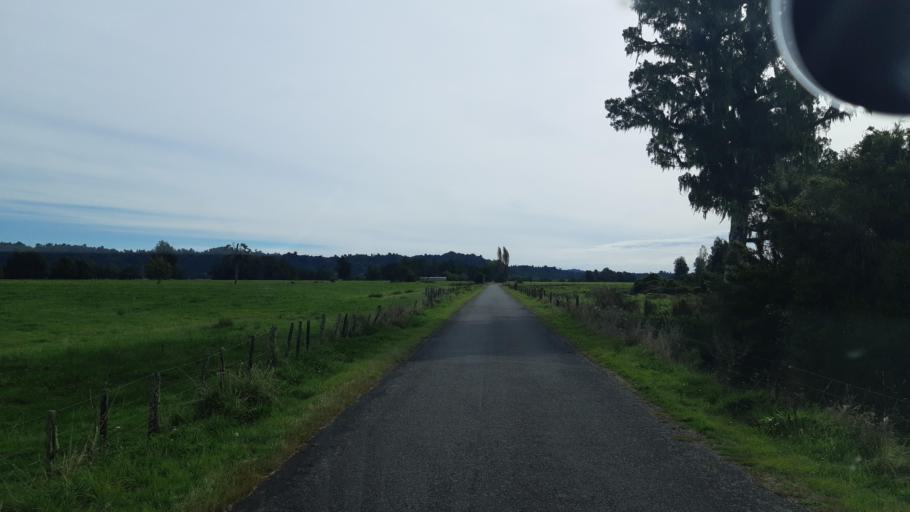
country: NZ
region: West Coast
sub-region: Westland District
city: Hokitika
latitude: -43.1281
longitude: 170.5013
